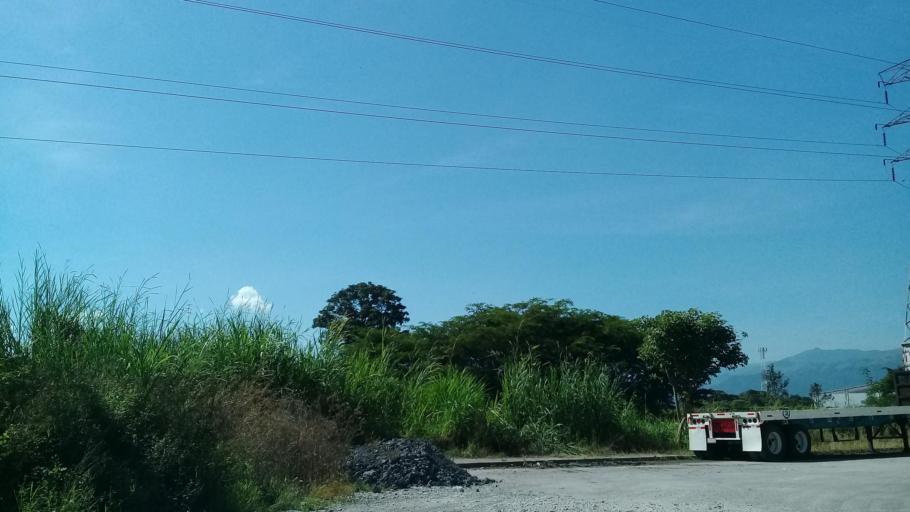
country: MX
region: Veracruz
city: Amatlan de los Reyes
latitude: 18.8574
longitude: -96.9092
